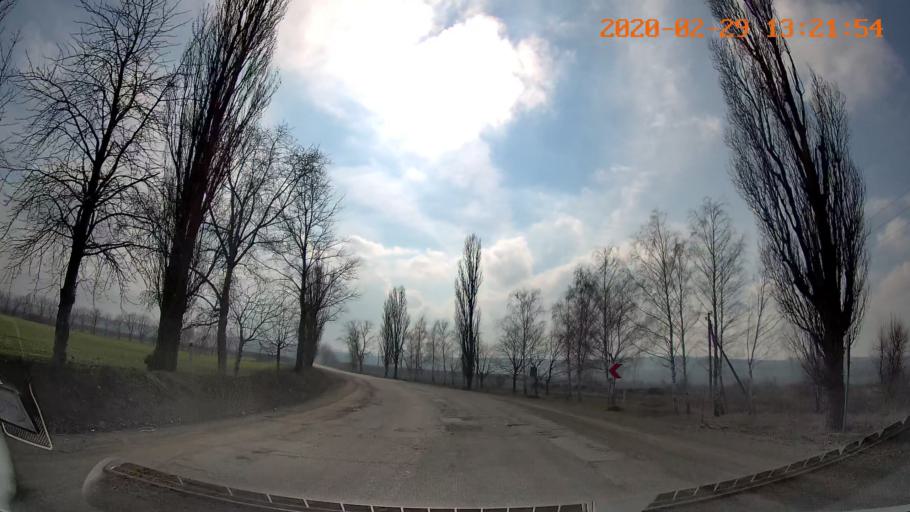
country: MD
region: Telenesti
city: Camenca
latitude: 47.9662
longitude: 28.6290
